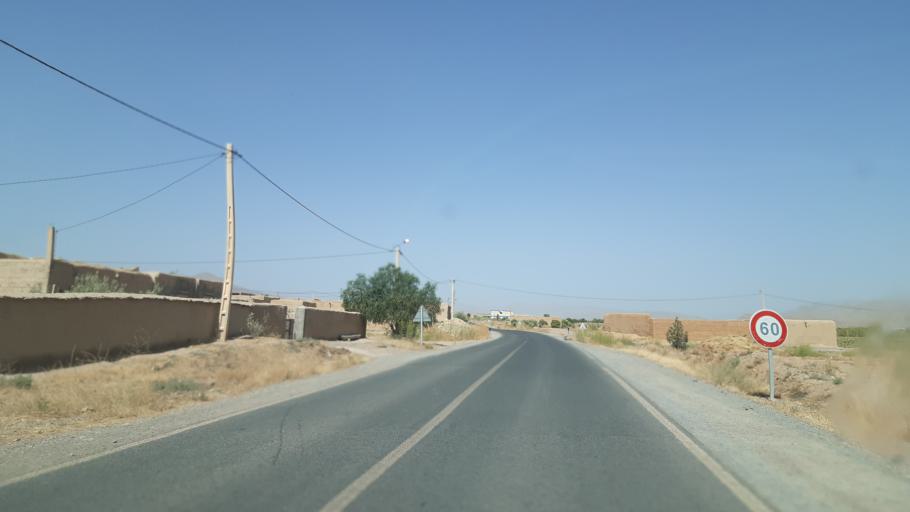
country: MA
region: Meknes-Tafilalet
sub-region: Errachidia
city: Amouguer
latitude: 32.2408
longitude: -4.5981
